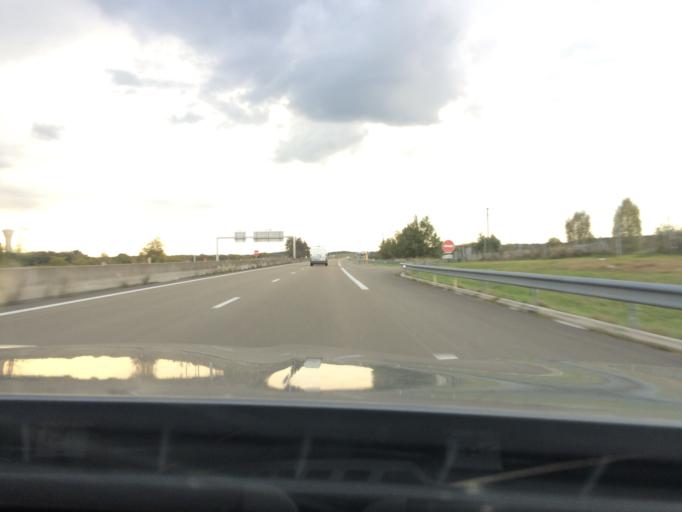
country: FR
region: Ile-de-France
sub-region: Departement de Seine-et-Marne
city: Souppes-sur-Loing
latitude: 48.2206
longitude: 2.7690
